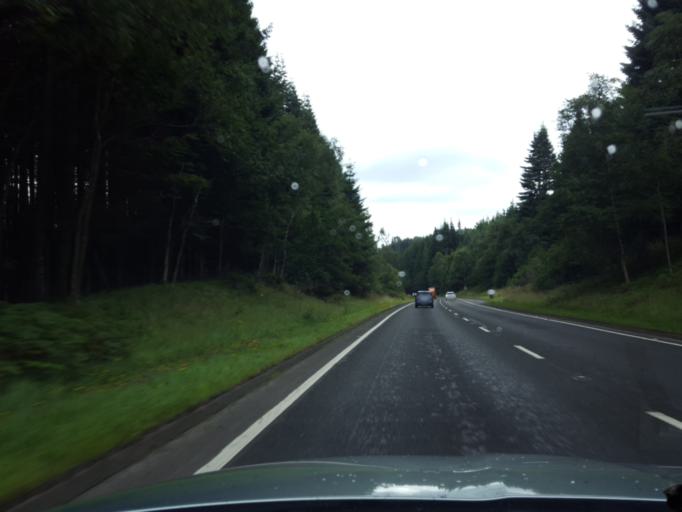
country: GB
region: Scotland
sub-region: Perth and Kinross
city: Bankfoot
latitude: 56.5446
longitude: -3.5535
